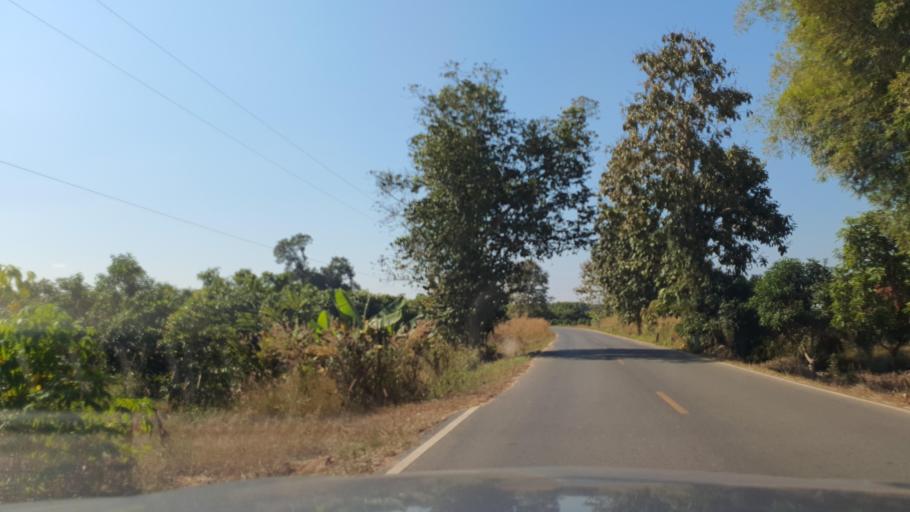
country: TH
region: Nan
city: Pua
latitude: 19.1288
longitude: 100.9240
